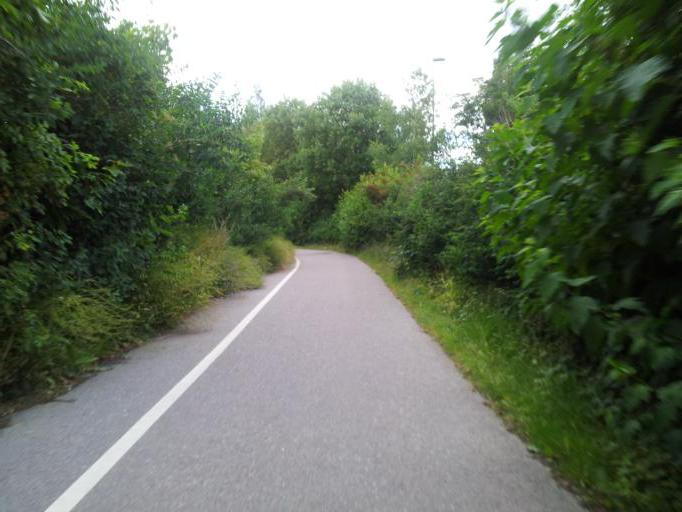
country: SE
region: Uppsala
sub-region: Uppsala Kommun
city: Gamla Uppsala
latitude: 59.8804
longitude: 17.6202
